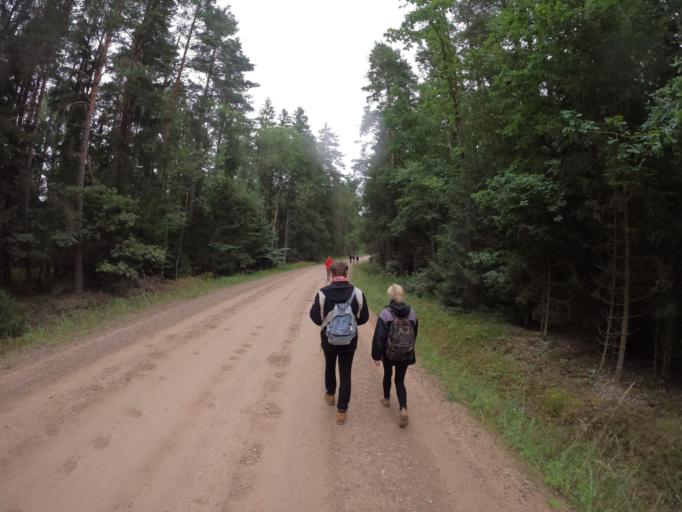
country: LV
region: Kuldigas Rajons
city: Kuldiga
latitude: 56.9931
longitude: 21.9752
